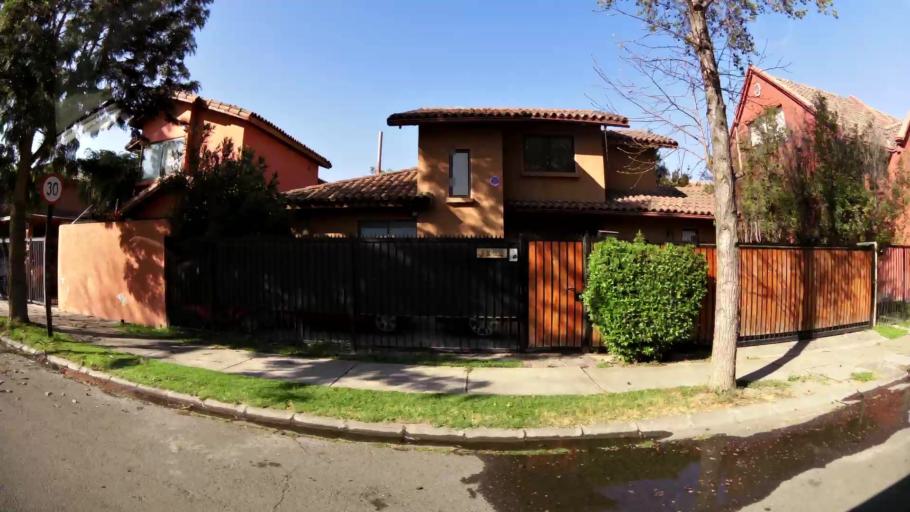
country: CL
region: Santiago Metropolitan
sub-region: Provincia de Chacabuco
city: Chicureo Abajo
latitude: -33.3559
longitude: -70.6669
